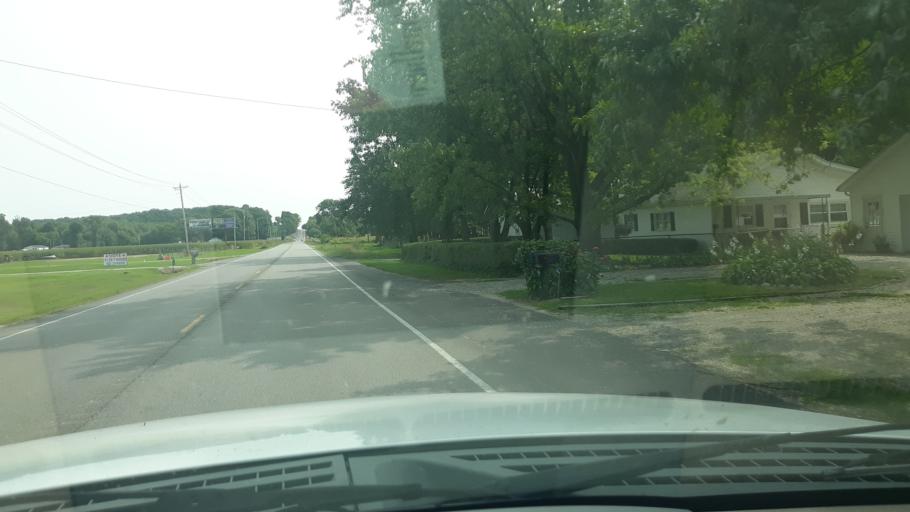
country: US
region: Indiana
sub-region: Gibson County
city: Owensville
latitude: 38.3559
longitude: -87.6696
